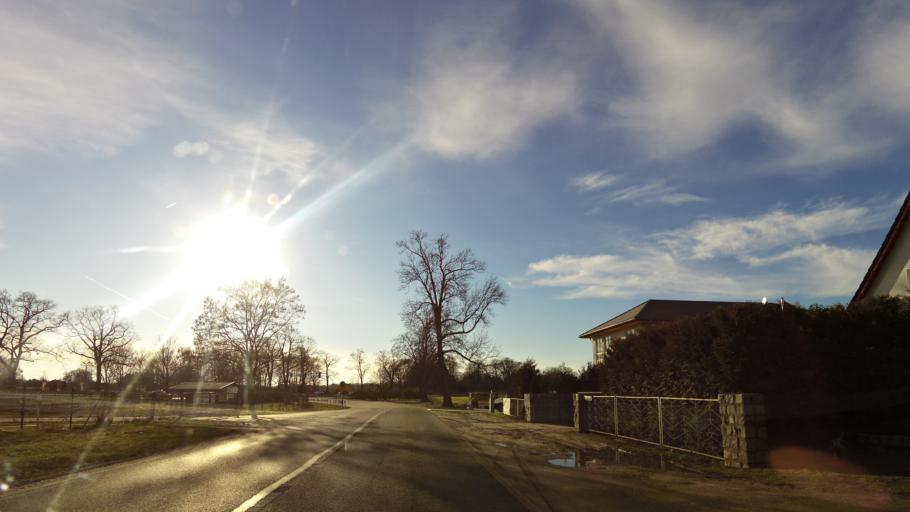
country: DE
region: Brandenburg
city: Schoneiche
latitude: 52.5017
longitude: 13.7213
